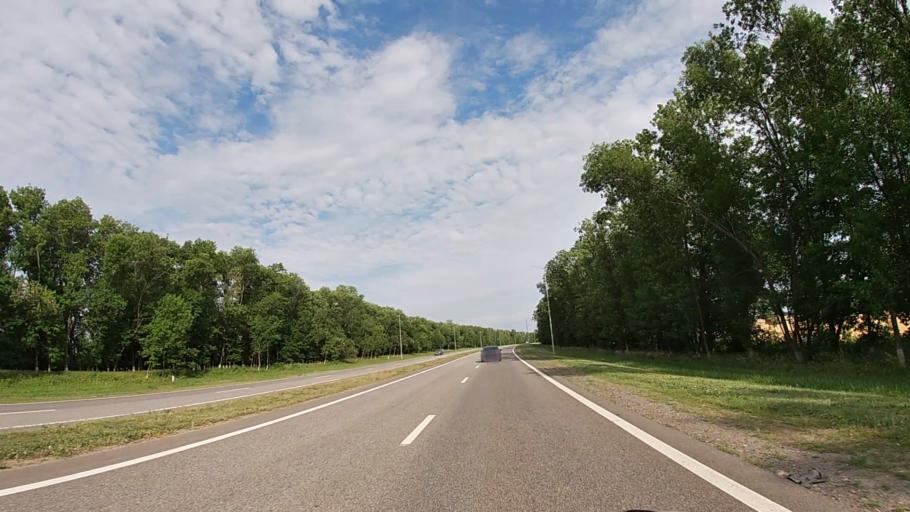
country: RU
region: Belgorod
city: Tomarovka
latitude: 50.6673
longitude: 36.3112
